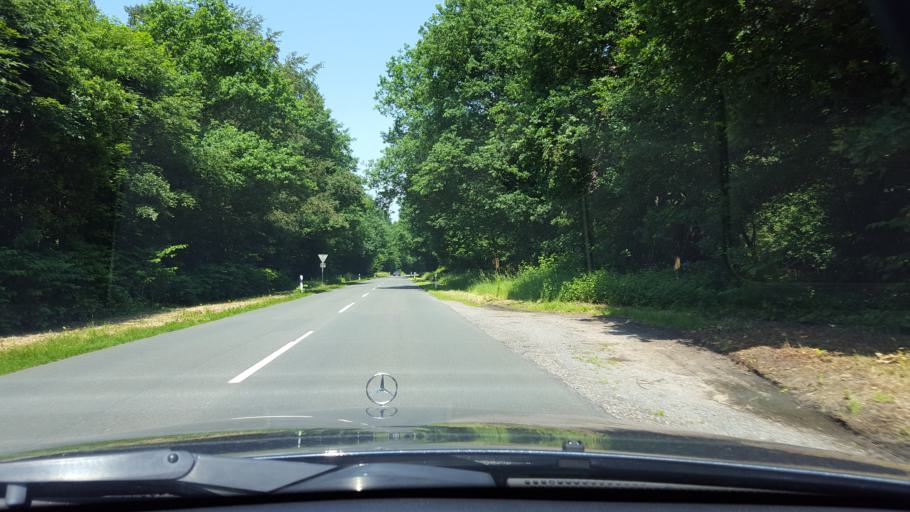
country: DE
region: North Rhine-Westphalia
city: Olfen
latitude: 51.7054
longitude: 7.3155
